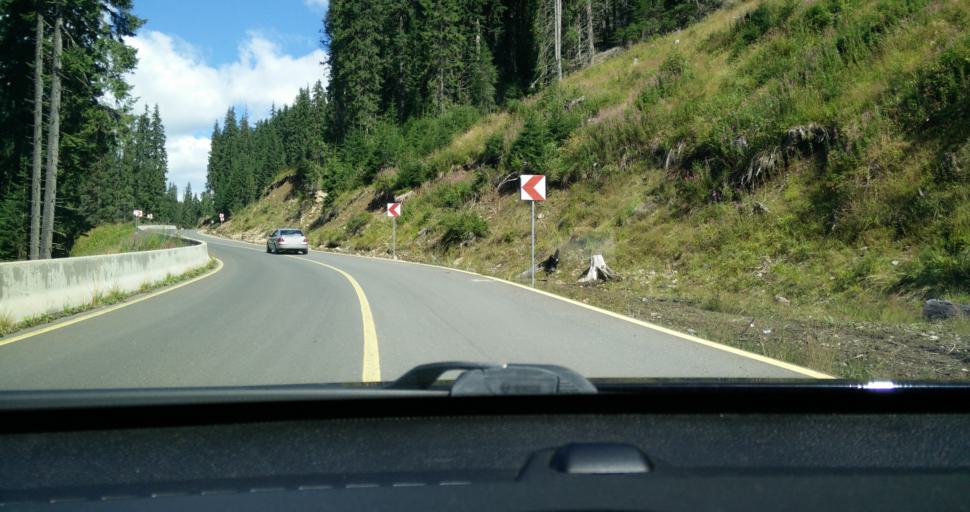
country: RO
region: Hunedoara
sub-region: Oras Petrila
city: Petrila
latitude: 45.4404
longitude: 23.6275
